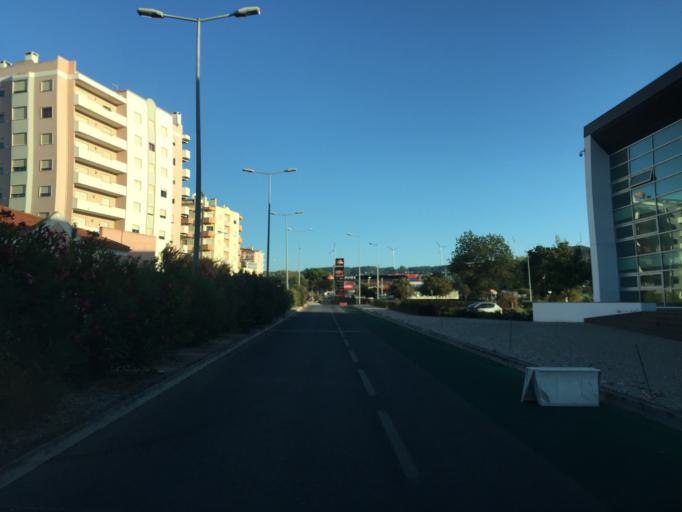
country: PT
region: Lisbon
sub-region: Torres Vedras
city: Torres Vedras
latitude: 39.0835
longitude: -9.2609
